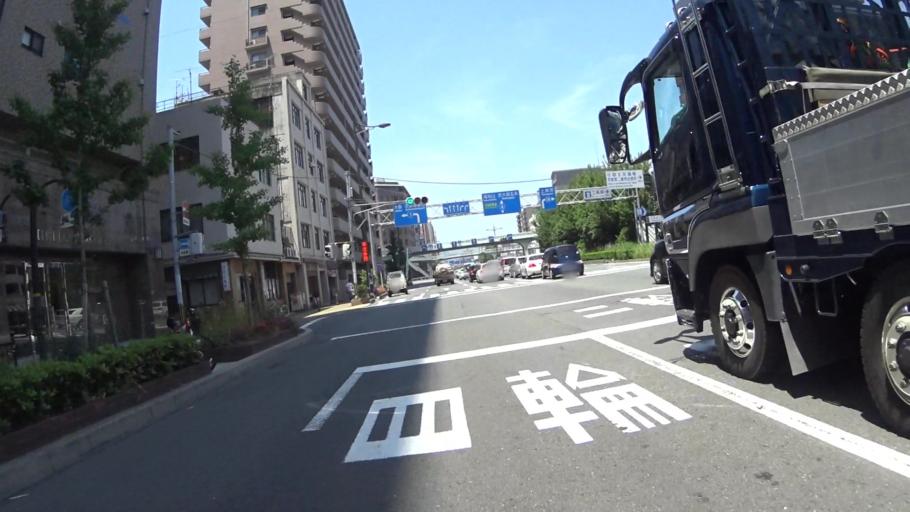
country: JP
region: Kyoto
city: Kyoto
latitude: 34.9961
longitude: 135.7536
